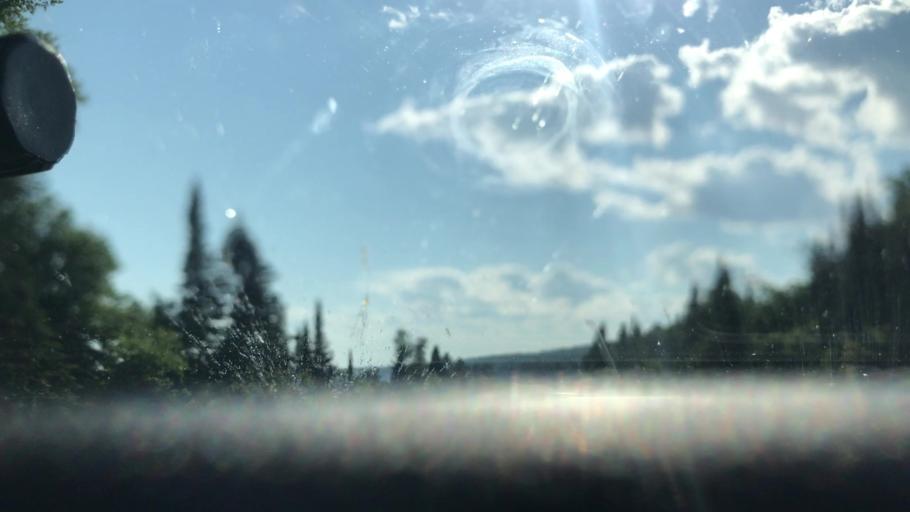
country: US
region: Minnesota
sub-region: Cook County
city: Grand Marais
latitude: 47.7953
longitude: -90.1428
